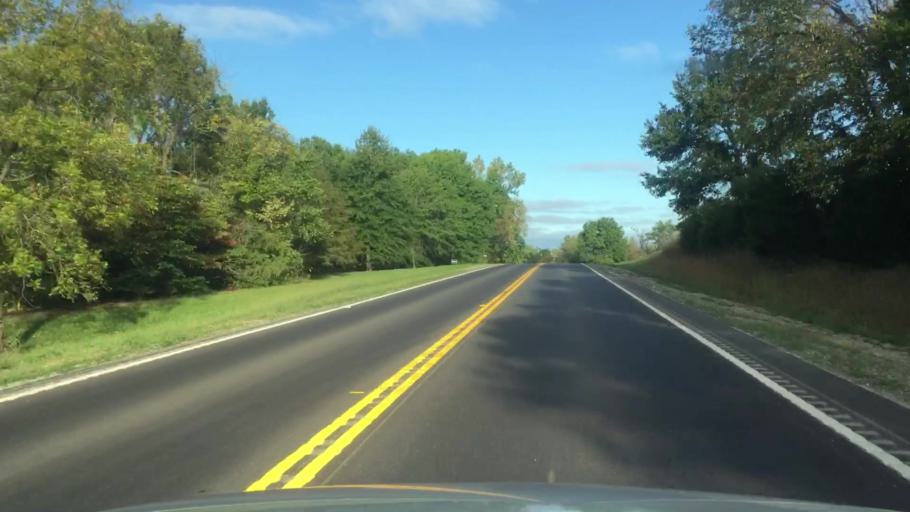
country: US
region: Missouri
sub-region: Howard County
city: New Franklin
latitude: 38.9907
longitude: -92.5610
